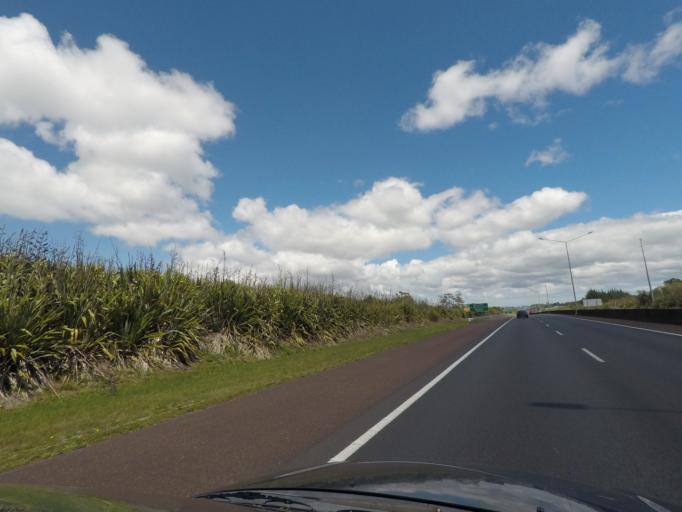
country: NZ
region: Auckland
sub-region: Auckland
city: Rosebank
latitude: -36.7958
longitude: 174.6463
